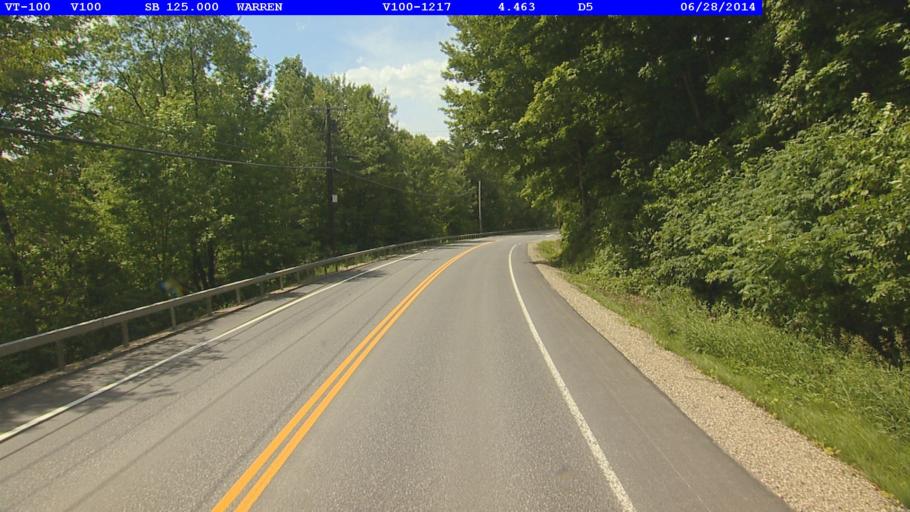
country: US
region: Vermont
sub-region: Washington County
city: Northfield
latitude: 44.1217
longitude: -72.8542
